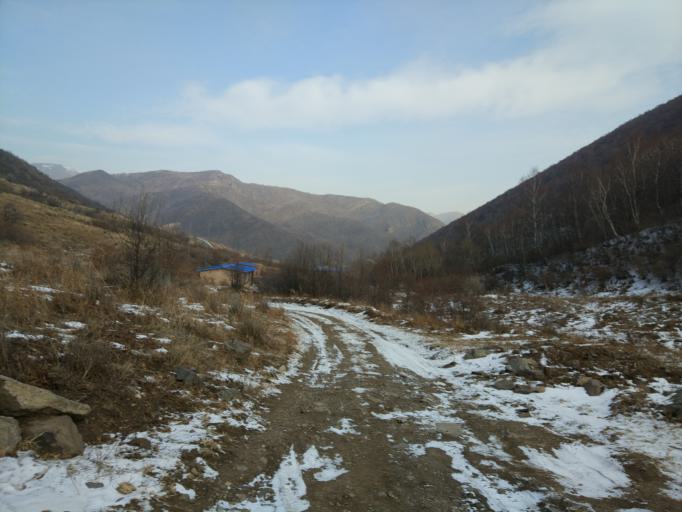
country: CN
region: Hebei
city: Xiwanzi
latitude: 40.8437
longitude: 115.4621
